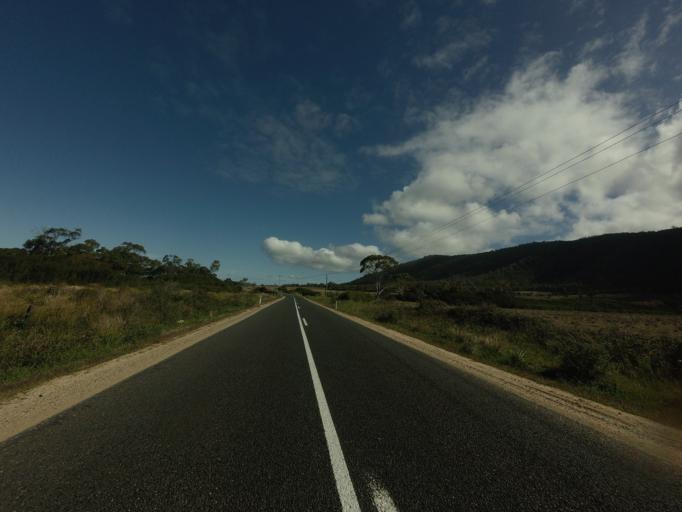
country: AU
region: Tasmania
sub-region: Break O'Day
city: St Helens
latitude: -41.7216
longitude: 148.2735
